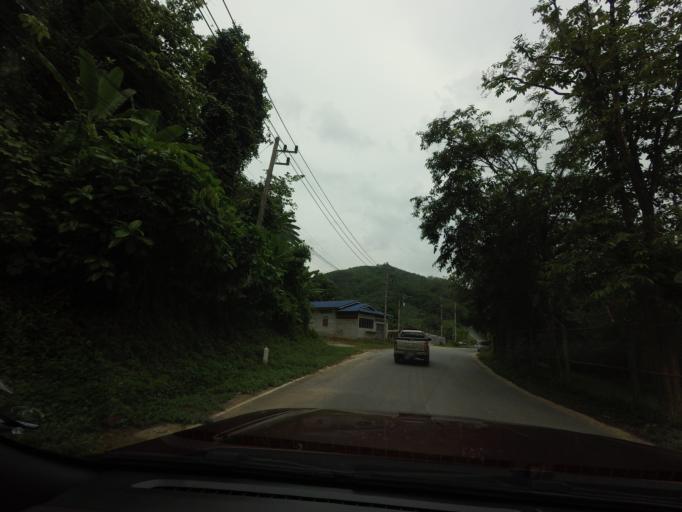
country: TH
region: Yala
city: Than To
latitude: 6.1567
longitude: 101.2797
